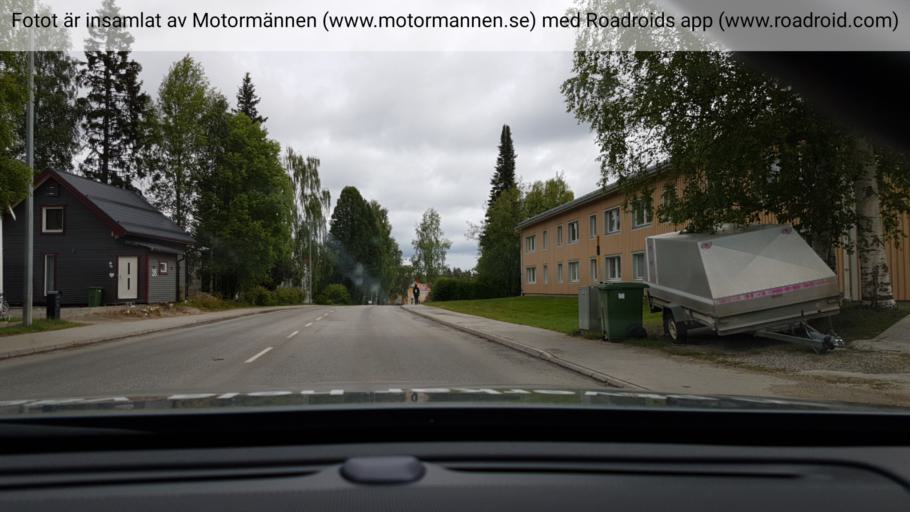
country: SE
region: Vaesterbotten
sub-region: Lycksele Kommun
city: Lycksele
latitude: 64.5880
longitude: 18.6656
